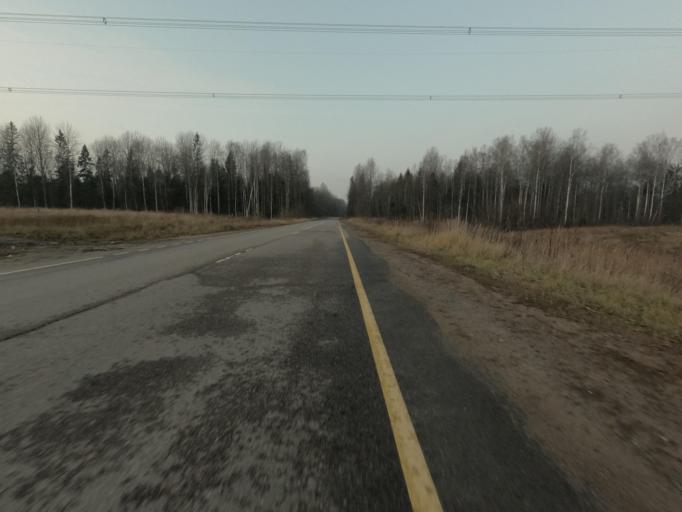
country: RU
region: Leningrad
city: Kirovsk
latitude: 59.8512
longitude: 30.9895
